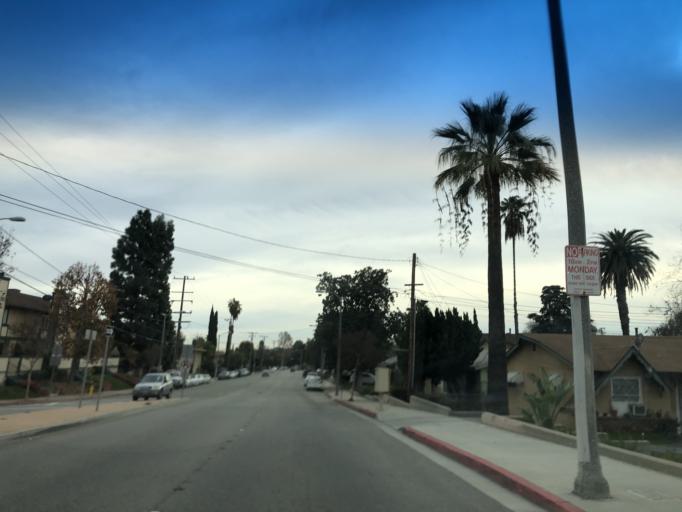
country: US
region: California
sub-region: Los Angeles County
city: Monrovia
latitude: 34.1349
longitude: -118.0096
